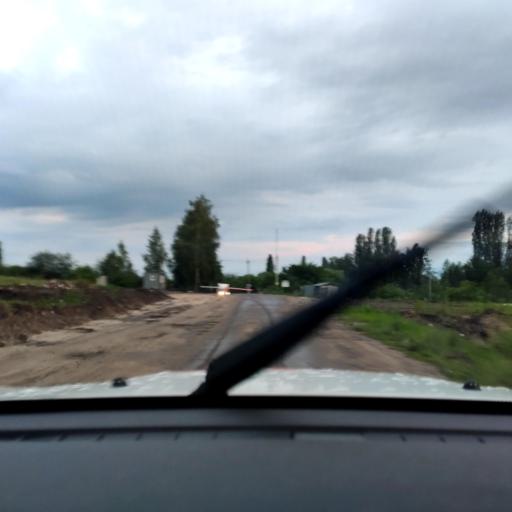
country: RU
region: Voronezj
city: Maslovka
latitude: 51.5150
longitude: 39.2272
